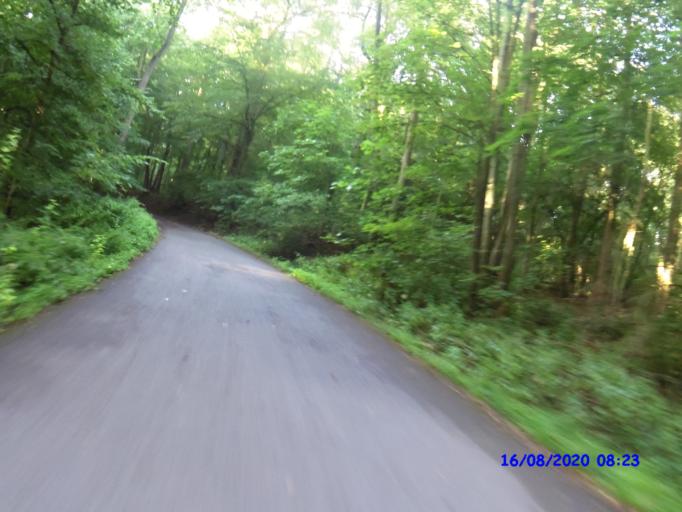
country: BE
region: Flanders
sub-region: Provincie Vlaams-Brabant
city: Sint-Genesius-Rode
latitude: 50.7931
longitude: 4.3994
